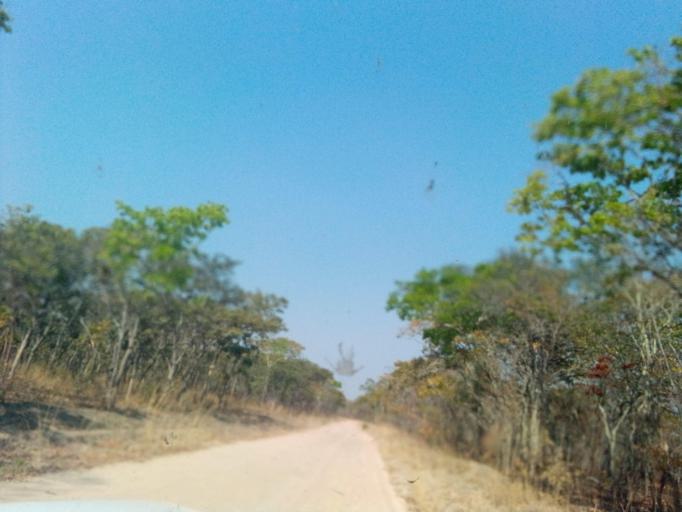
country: ZM
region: Northern
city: Mpika
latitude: -12.2272
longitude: 30.8902
